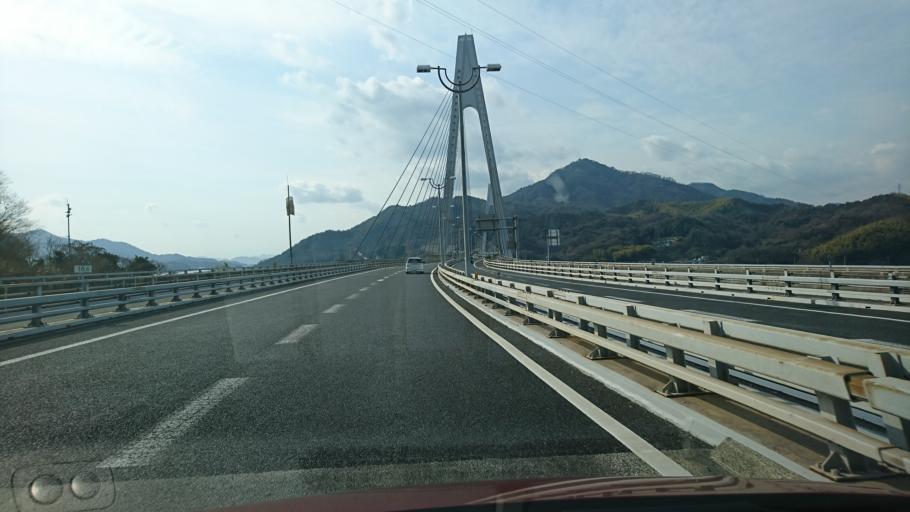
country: JP
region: Hiroshima
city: Innoshima
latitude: 34.3071
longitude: 133.1541
